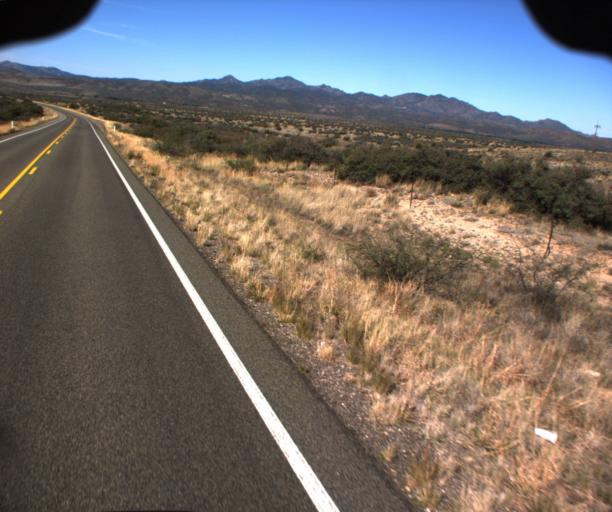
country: US
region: Arizona
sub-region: Yavapai County
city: Prescott
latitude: 34.3842
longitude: -112.6523
